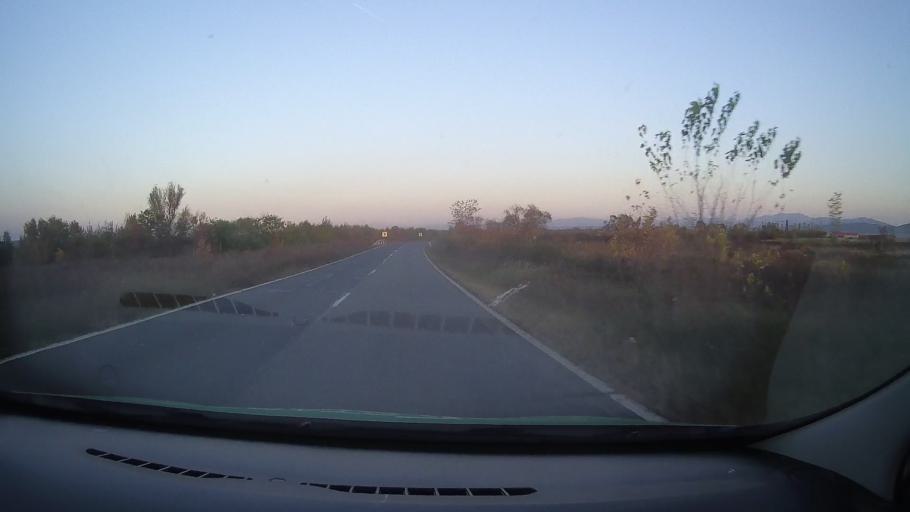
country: RO
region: Timis
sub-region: Comuna Dumbrava
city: Rachita
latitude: 45.8246
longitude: 22.0914
